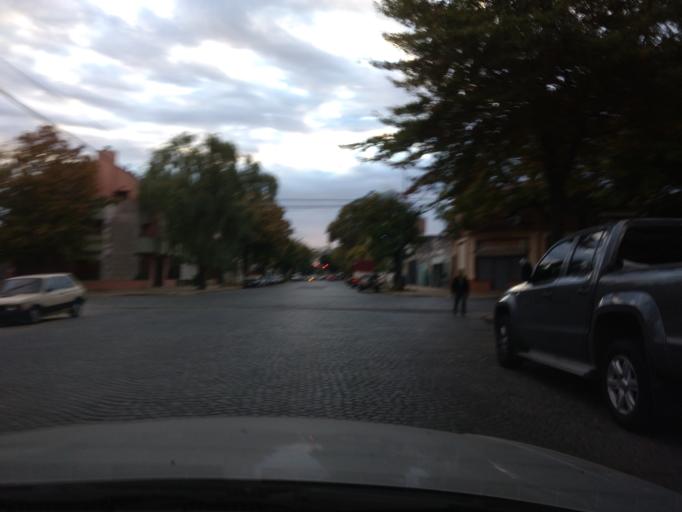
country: AR
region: Buenos Aires F.D.
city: Villa Santa Rita
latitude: -34.6322
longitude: -58.4949
